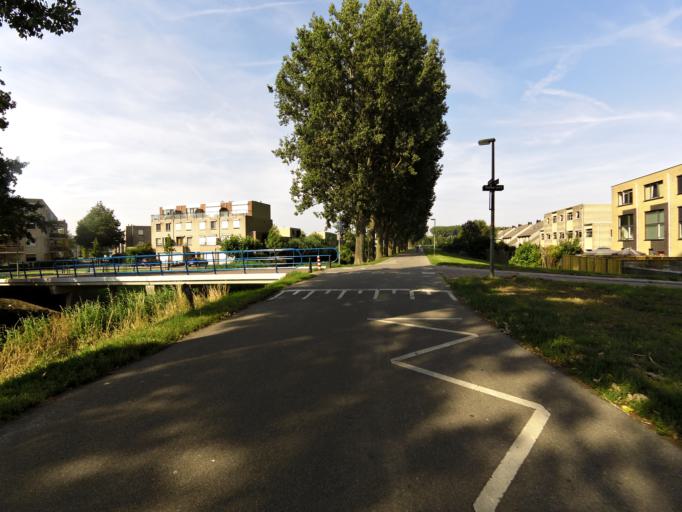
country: NL
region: South Holland
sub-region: Gemeente Papendrecht
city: Papendrecht
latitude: 51.8041
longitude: 4.7153
